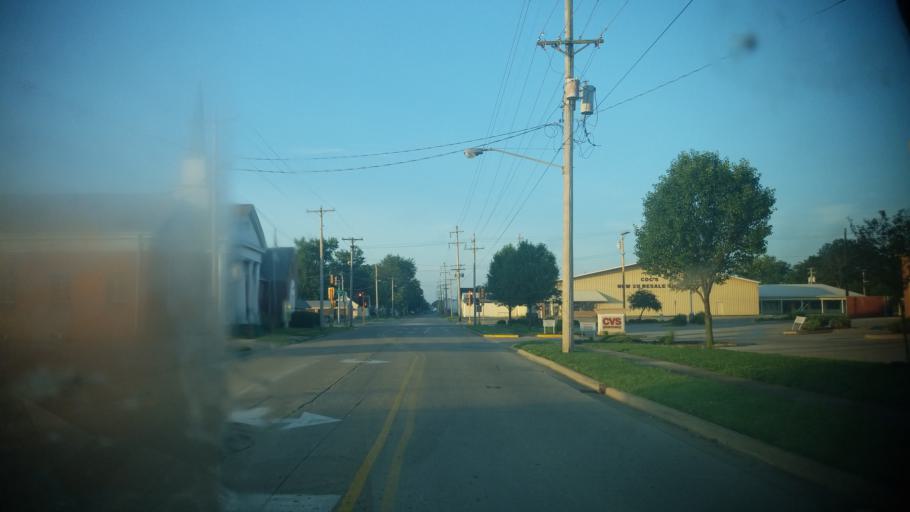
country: US
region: Illinois
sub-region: Wayne County
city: Fairfield
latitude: 38.3796
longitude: -88.3685
